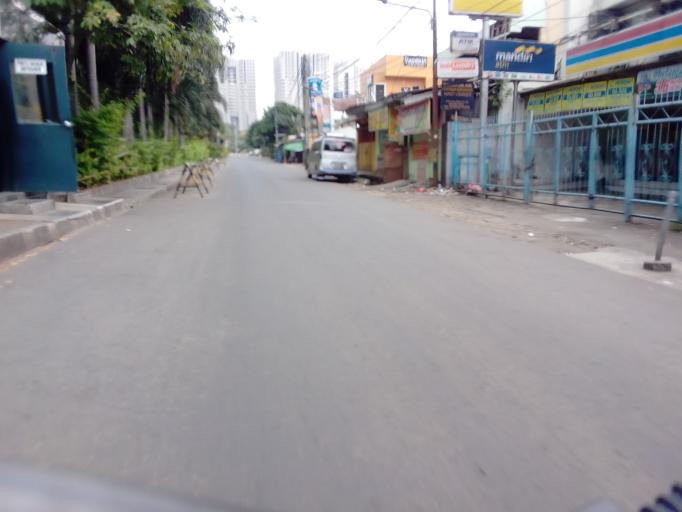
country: ID
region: Jakarta Raya
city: Jakarta
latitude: -6.2169
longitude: 106.8129
